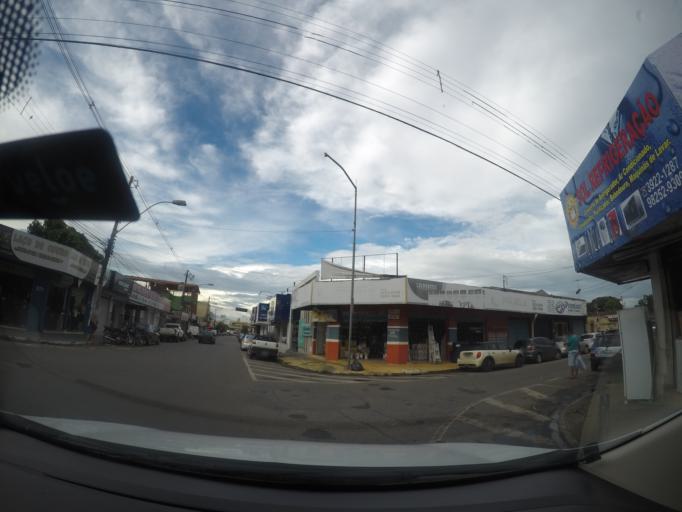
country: BR
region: Goias
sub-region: Goiania
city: Goiania
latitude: -16.6690
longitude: -49.2854
